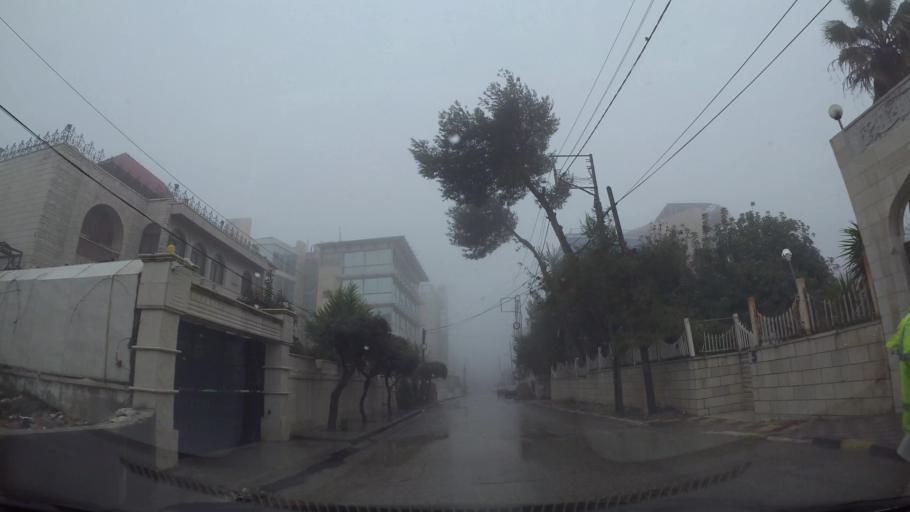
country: JO
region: Amman
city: Wadi as Sir
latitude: 31.9681
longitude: 35.8748
